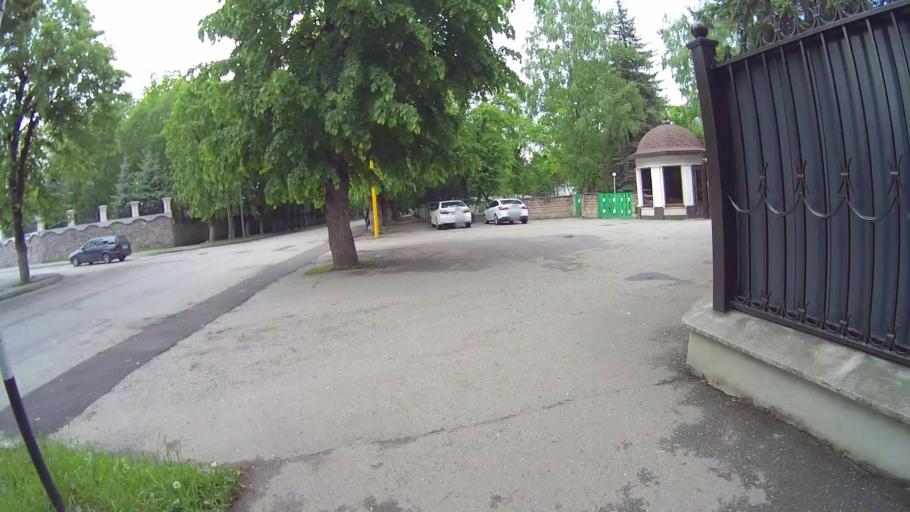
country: RU
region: Kabardino-Balkariya
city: Vol'nyy Aul
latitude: 43.4676
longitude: 43.5871
